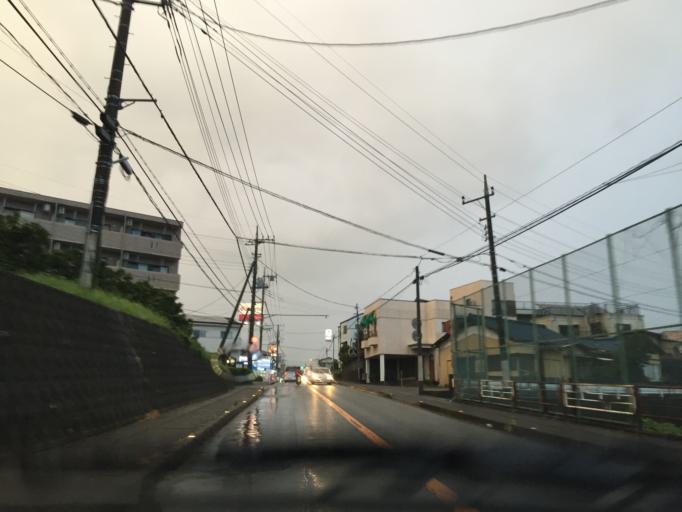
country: JP
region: Shizuoka
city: Mishima
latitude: 35.1442
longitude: 138.9105
